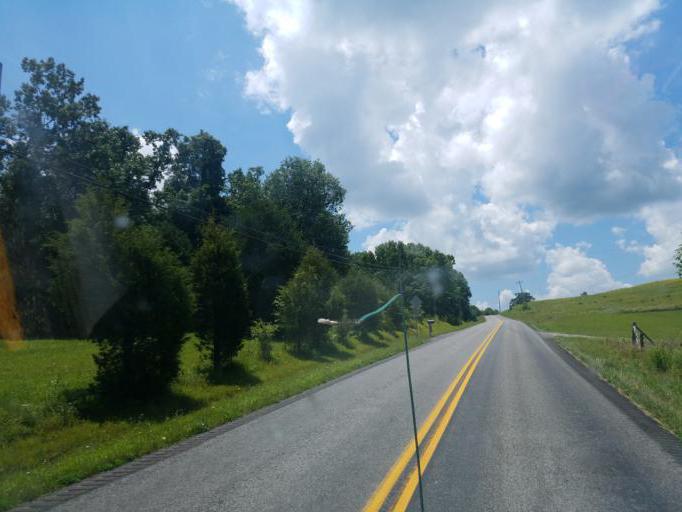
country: US
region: Kentucky
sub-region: Grayson County
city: Leitchfield
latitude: 37.4986
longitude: -86.4755
